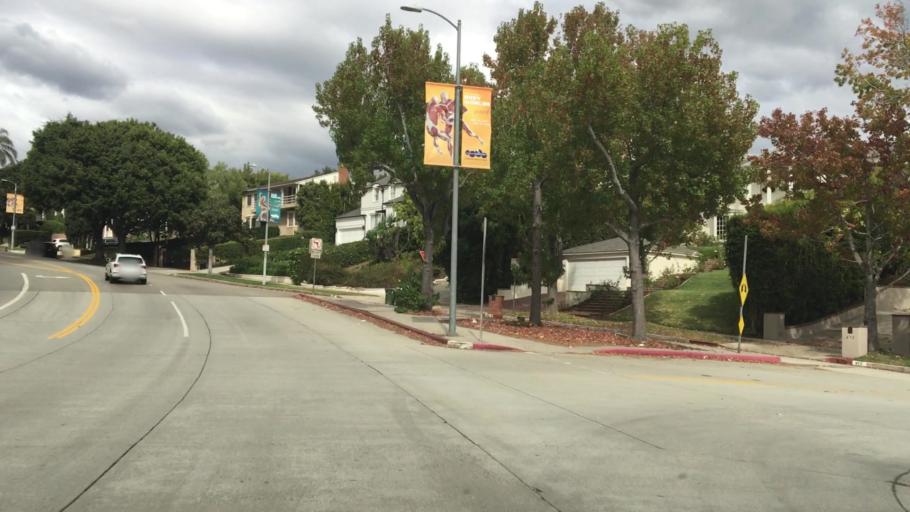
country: US
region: California
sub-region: Los Angeles County
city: Westwood, Los Angeles
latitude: 34.0722
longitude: -118.4372
